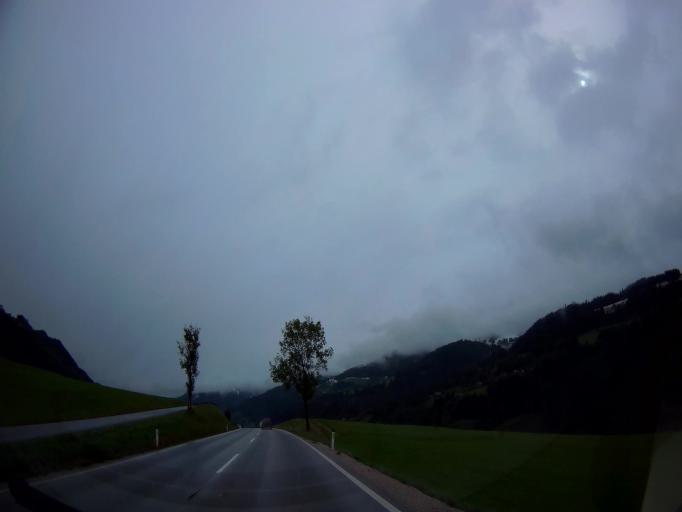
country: AT
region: Styria
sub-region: Politischer Bezirk Liezen
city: Pruggern
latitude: 47.4227
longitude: 13.8582
